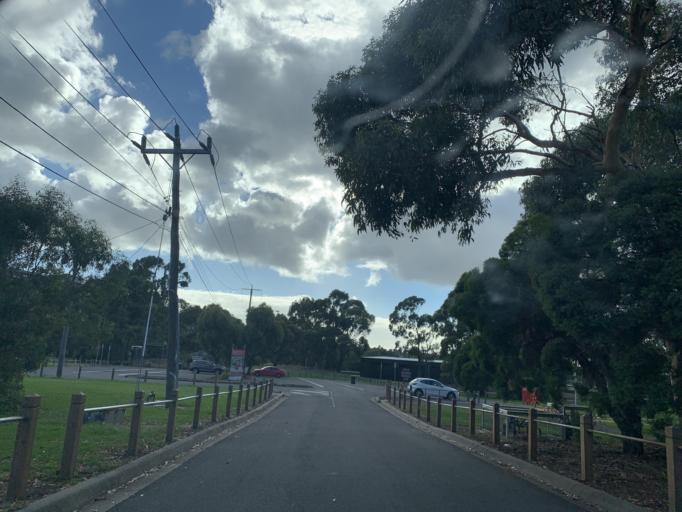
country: AU
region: Victoria
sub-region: Moreland
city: Gowanbrae
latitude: -37.7144
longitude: 144.9001
